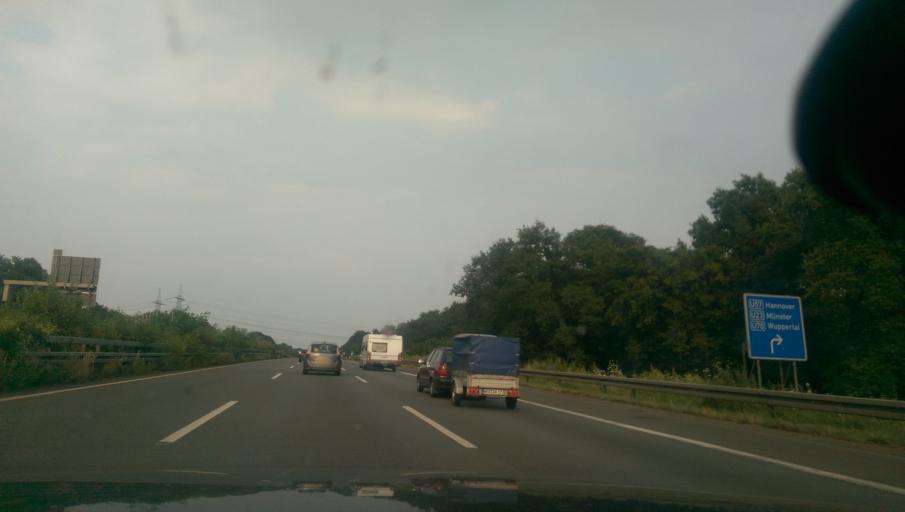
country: DE
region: North Rhine-Westphalia
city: Herten
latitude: 51.5707
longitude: 7.1208
